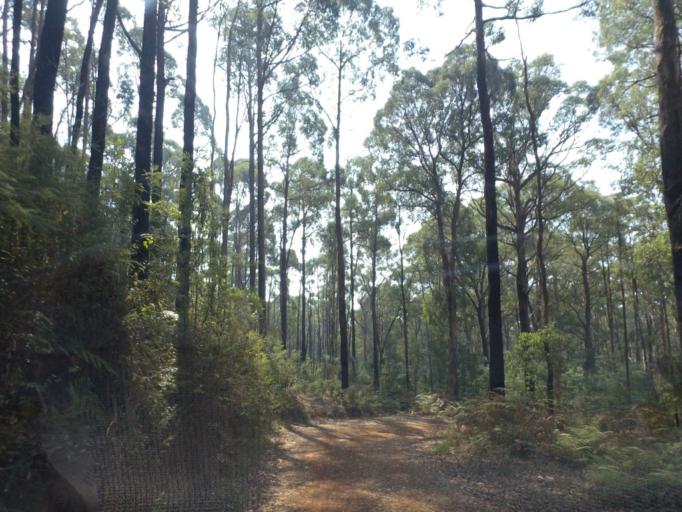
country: AU
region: Victoria
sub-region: Yarra Ranges
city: Millgrove
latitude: -37.5742
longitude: 145.6881
